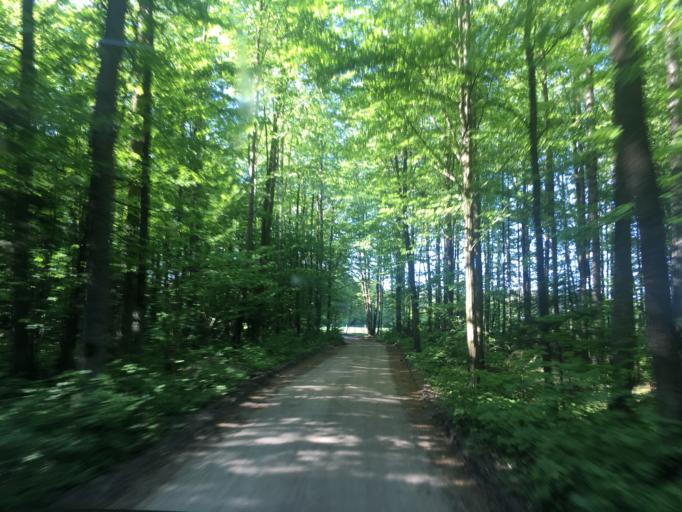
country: PL
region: Warmian-Masurian Voivodeship
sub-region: Powiat piski
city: Ruciane-Nida
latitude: 53.6524
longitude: 21.4850
